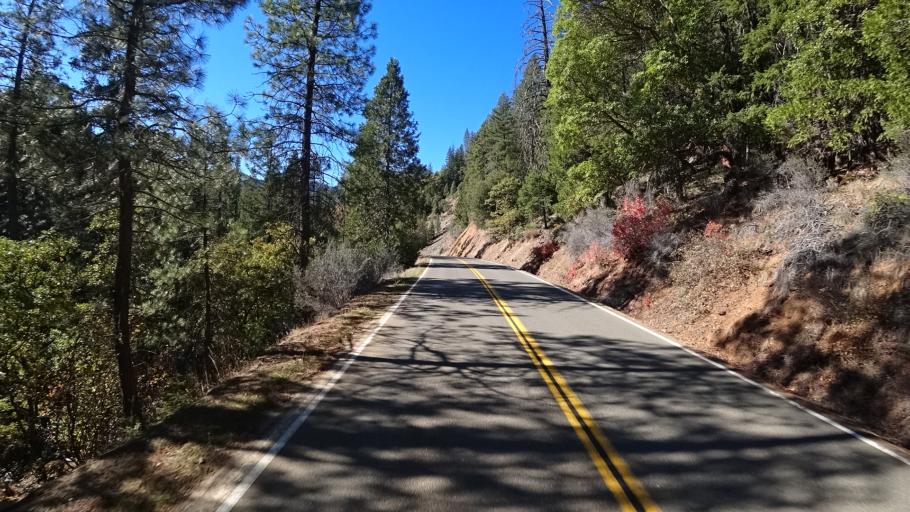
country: US
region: California
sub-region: Trinity County
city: Weaverville
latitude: 41.1443
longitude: -123.1239
